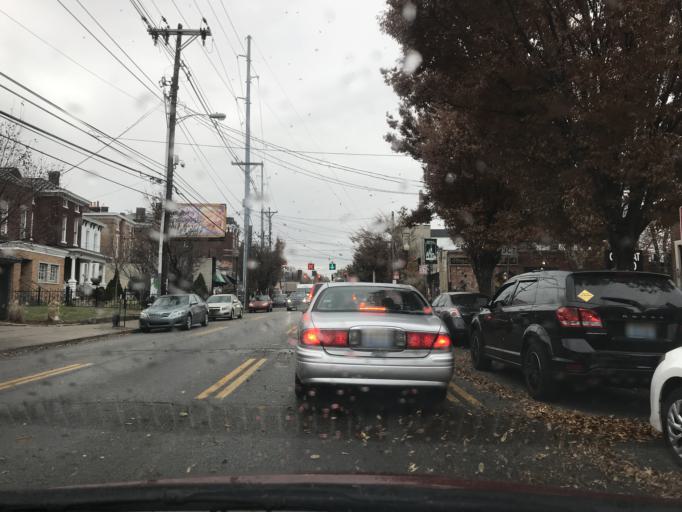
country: US
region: Kentucky
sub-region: Jefferson County
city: Louisville
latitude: 38.2411
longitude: -85.7250
